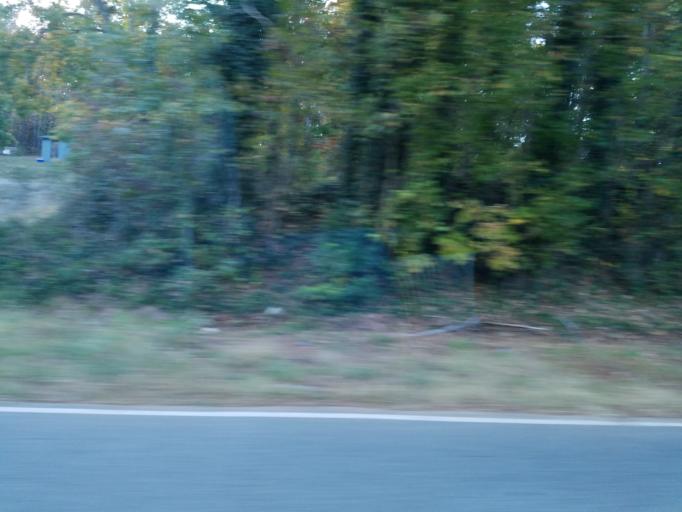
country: US
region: Georgia
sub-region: Bartow County
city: Adairsville
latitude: 34.3027
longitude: -84.9384
